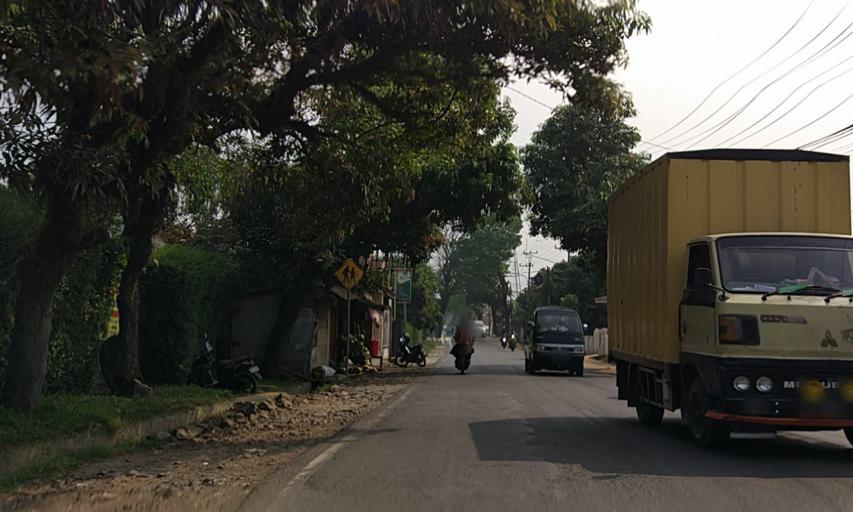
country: ID
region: West Java
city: Banjaran
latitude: -7.0439
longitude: 107.5627
